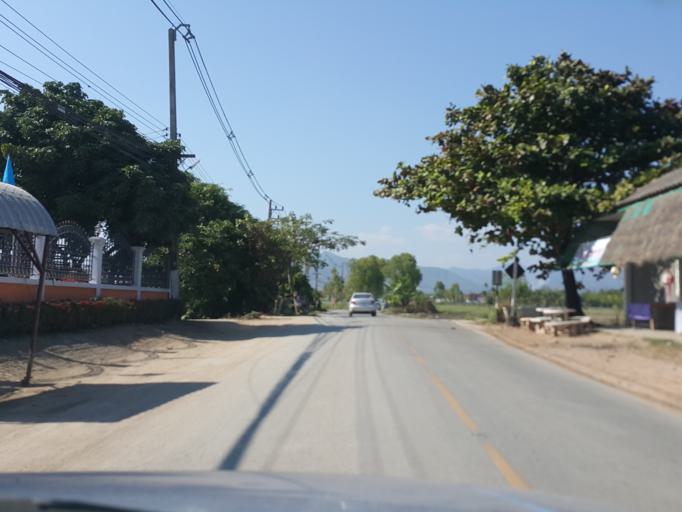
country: TH
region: Chiang Mai
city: Mae Wang
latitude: 18.6003
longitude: 98.8020
